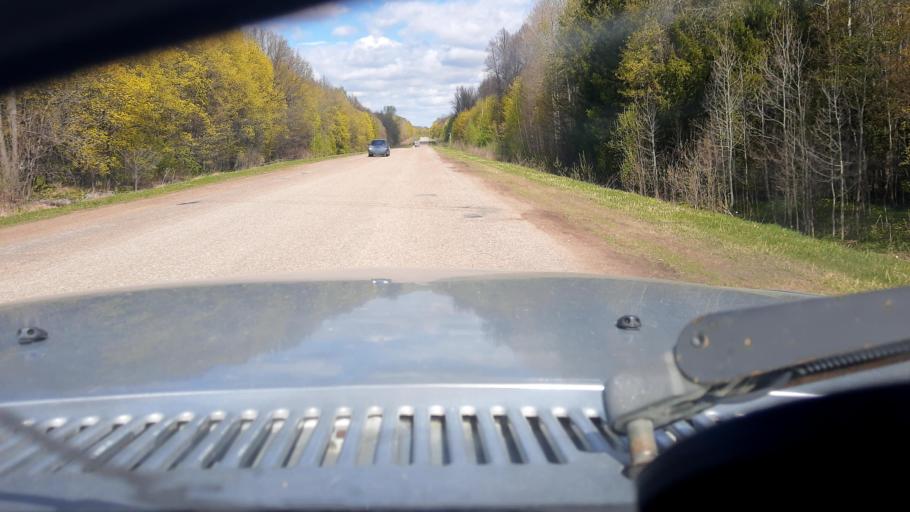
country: RU
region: Bashkortostan
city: Blagoveshchensk
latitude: 55.0992
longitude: 56.0602
